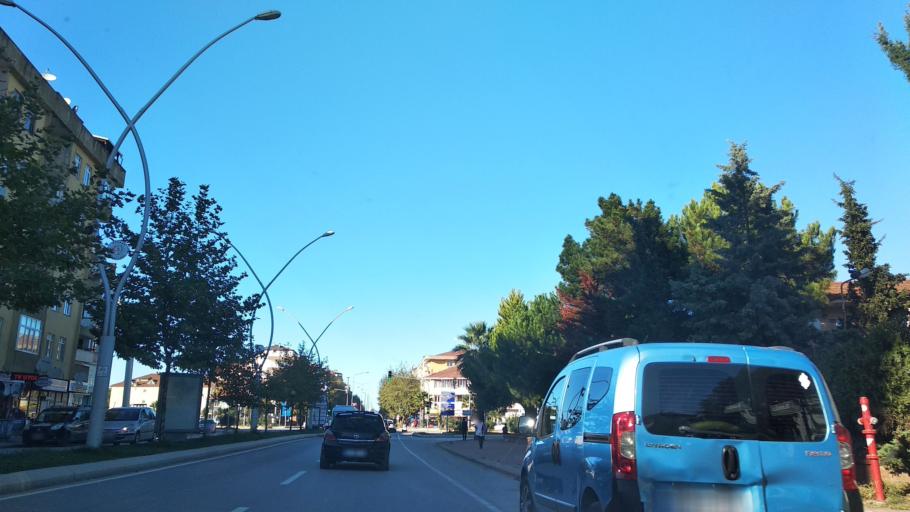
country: TR
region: Sakarya
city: Karasu
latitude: 41.1042
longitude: 30.6927
